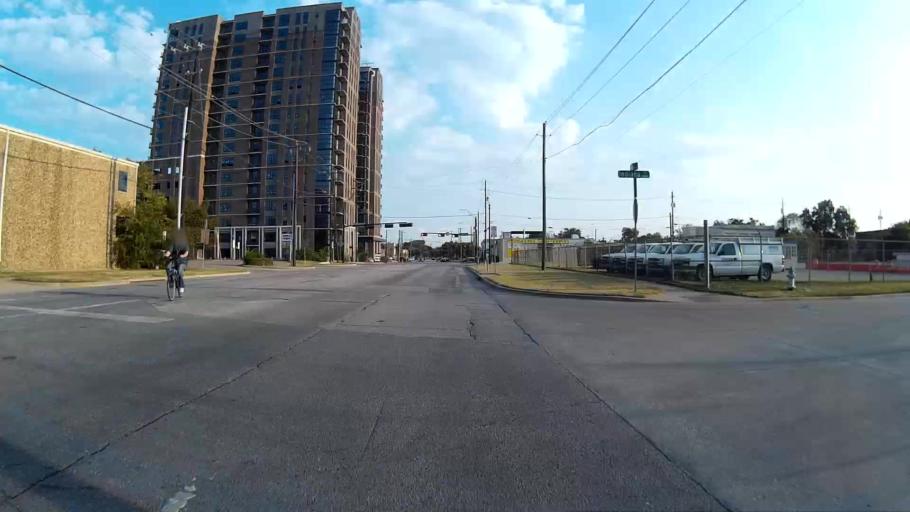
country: US
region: Texas
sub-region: Dallas County
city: Dallas
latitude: 32.7863
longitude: -96.7794
